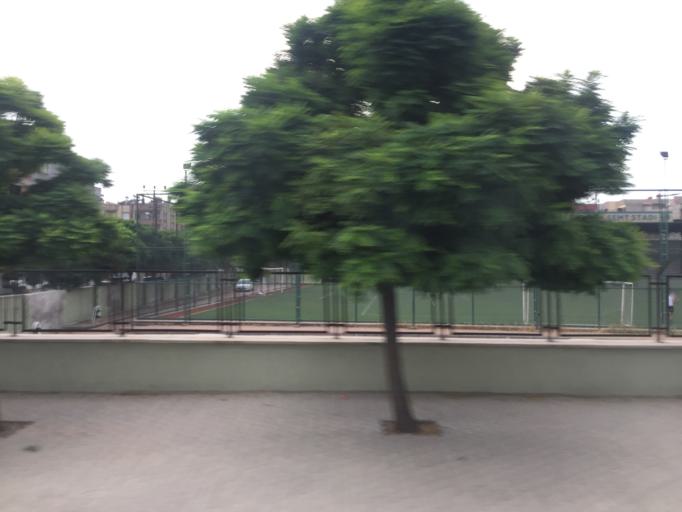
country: TR
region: Gaziantep
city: Gaziantep
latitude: 37.0645
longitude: 37.4150
